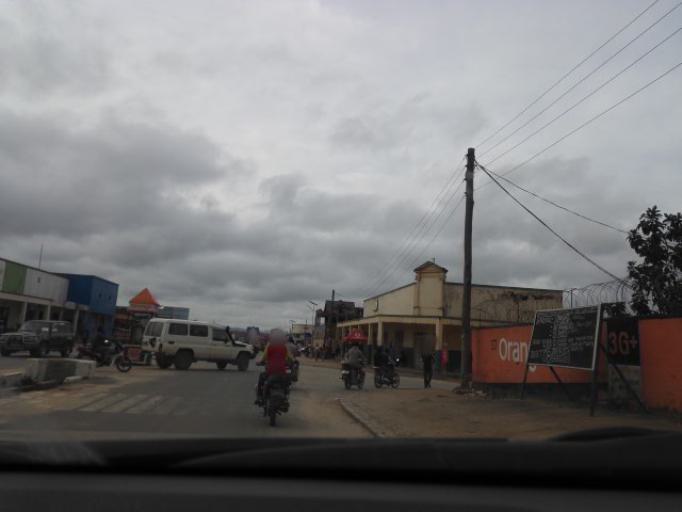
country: CD
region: Eastern Province
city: Bunia
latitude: 1.5552
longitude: 30.2479
